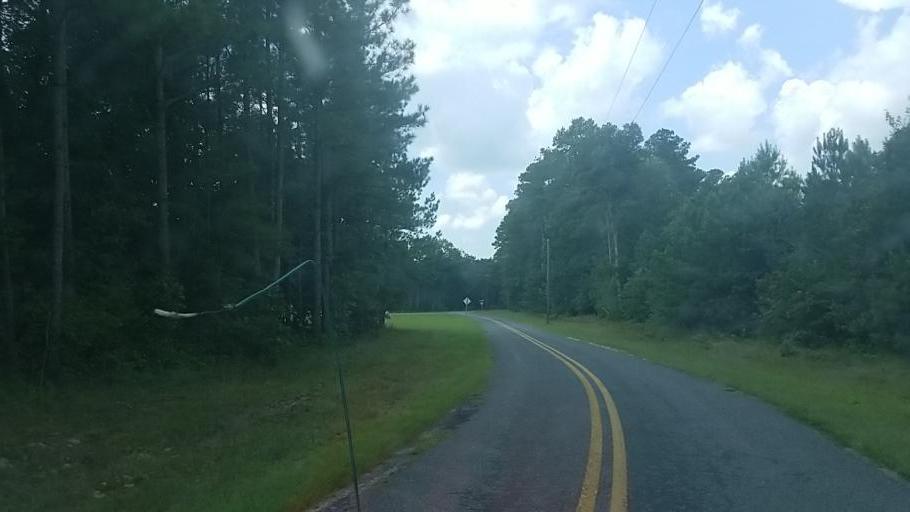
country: US
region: Maryland
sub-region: Worcester County
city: Snow Hill
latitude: 38.2561
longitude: -75.4419
